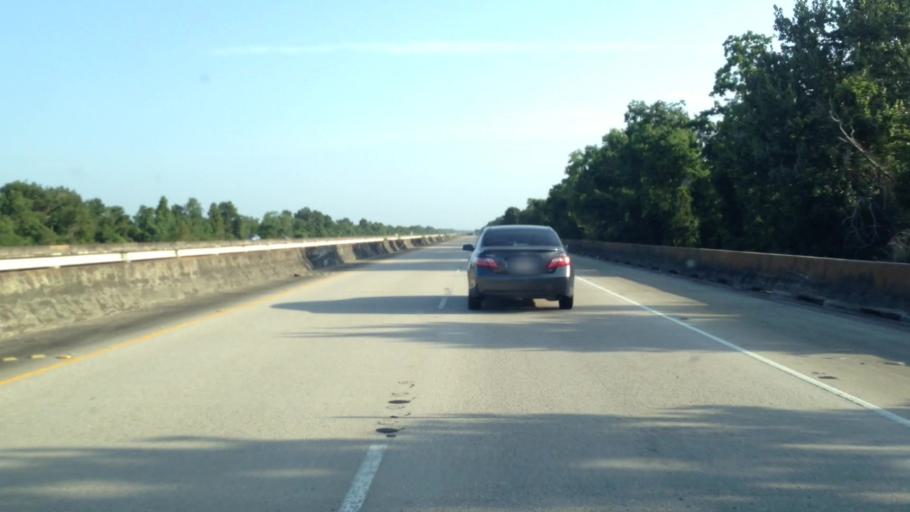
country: US
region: Louisiana
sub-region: Tangipahoa Parish
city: Ponchatoula
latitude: 30.3610
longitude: -90.4191
